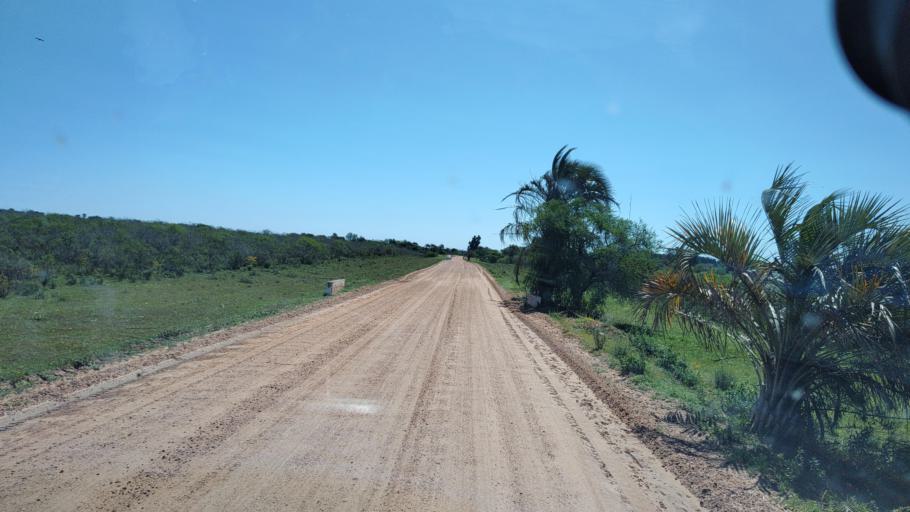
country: AR
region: Entre Rios
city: Ubajay
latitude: -31.8661
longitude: -58.2554
